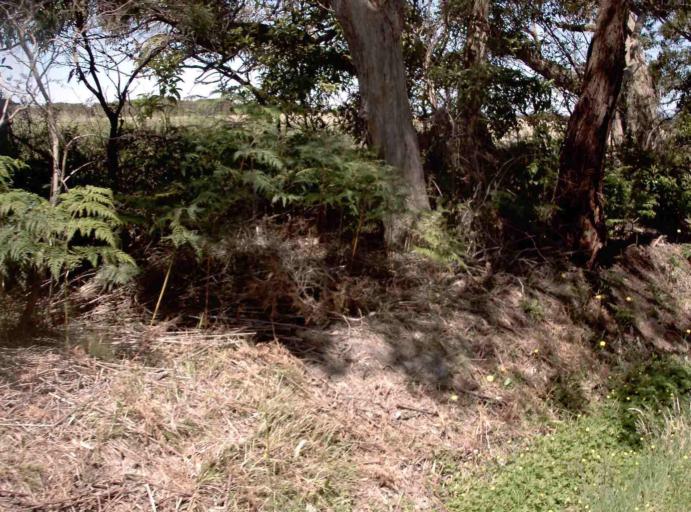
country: AU
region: Victoria
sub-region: Bass Coast
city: North Wonthaggi
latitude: -38.7785
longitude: 146.0772
